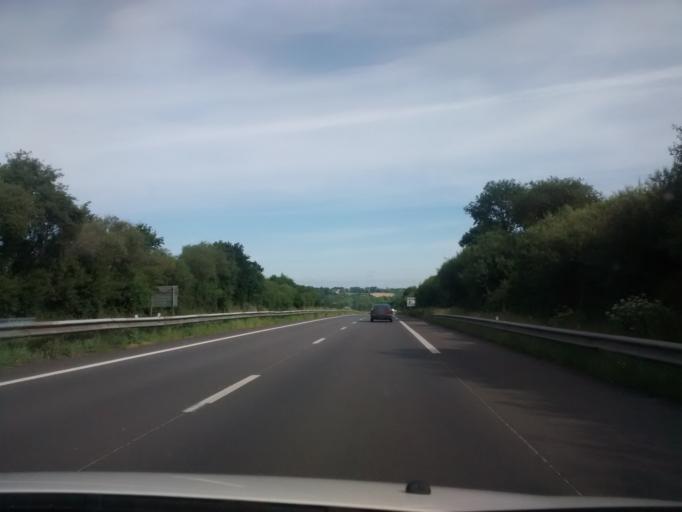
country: FR
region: Brittany
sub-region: Departement d'Ille-et-Vilaine
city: Quedillac
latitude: 48.2600
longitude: -2.1433
